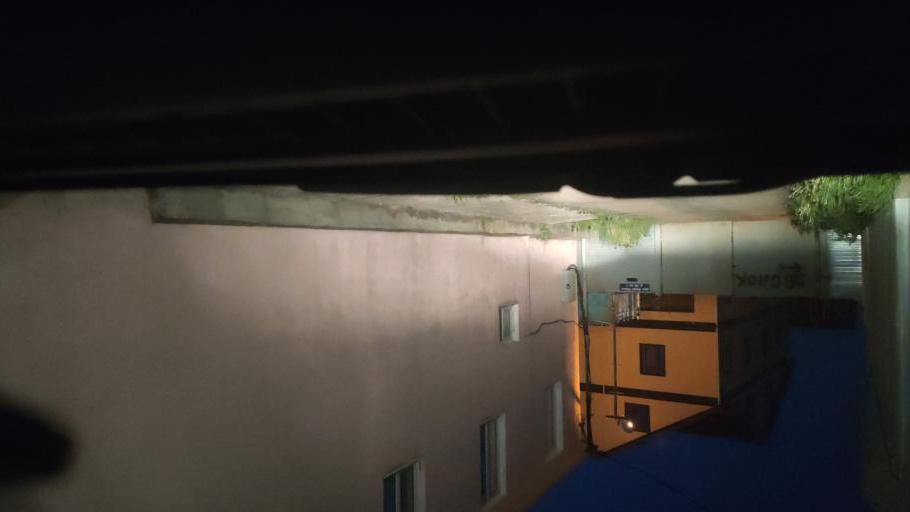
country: RU
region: Perm
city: Kondratovo
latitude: 58.0141
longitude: 56.0617
